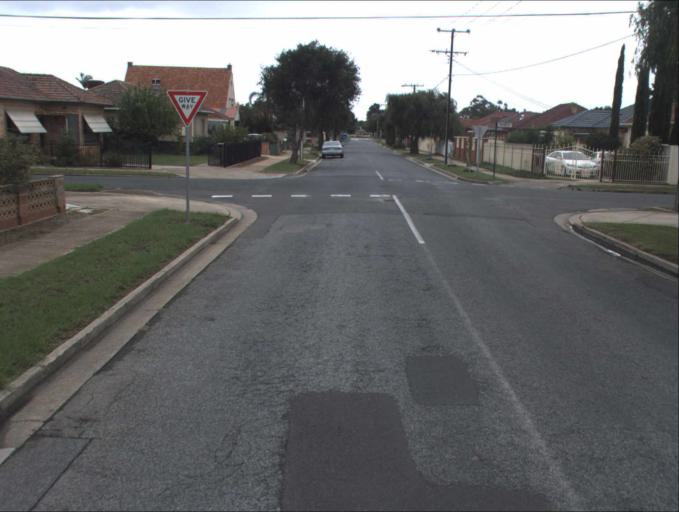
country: AU
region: South Australia
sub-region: Charles Sturt
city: Woodville
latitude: -34.8704
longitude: 138.5586
